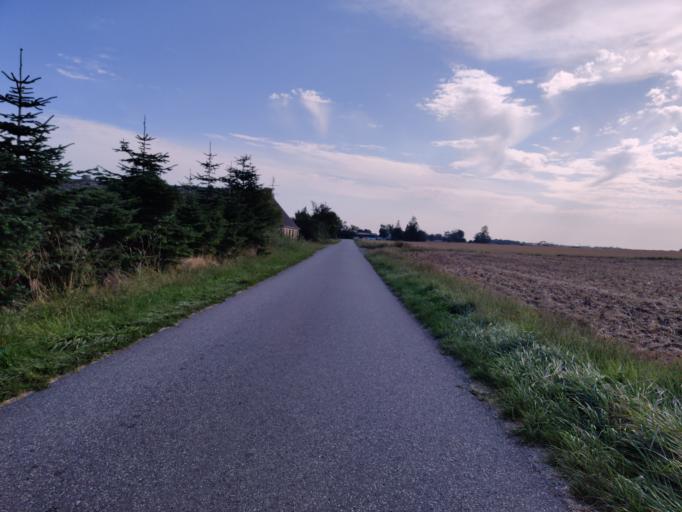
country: DK
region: Zealand
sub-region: Guldborgsund Kommune
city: Nykobing Falster
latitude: 54.6993
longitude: 11.9307
